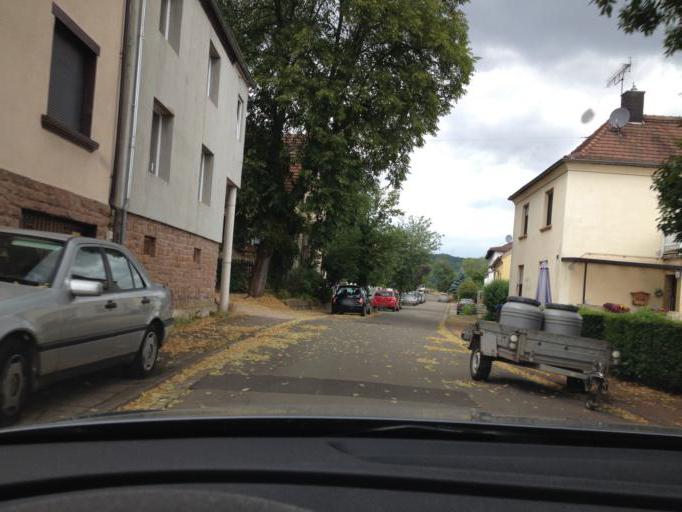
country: DE
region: Saarland
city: Ottweiler
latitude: 49.4325
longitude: 7.1563
